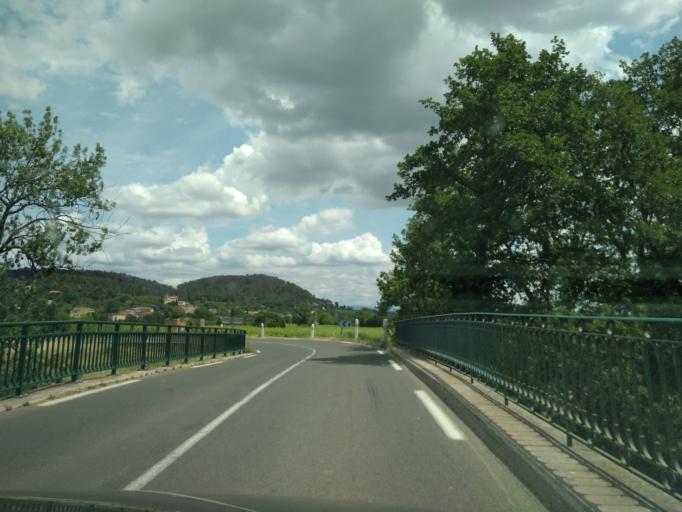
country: FR
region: Provence-Alpes-Cote d'Azur
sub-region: Departement du Var
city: Le Val
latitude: 43.4671
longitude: 6.1140
